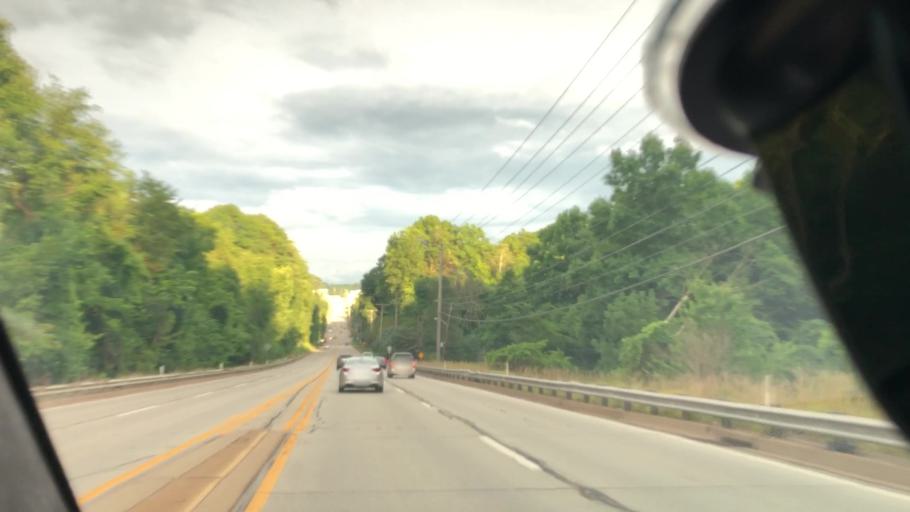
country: US
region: Pennsylvania
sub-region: Allegheny County
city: Churchill
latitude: 40.4372
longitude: -79.8283
